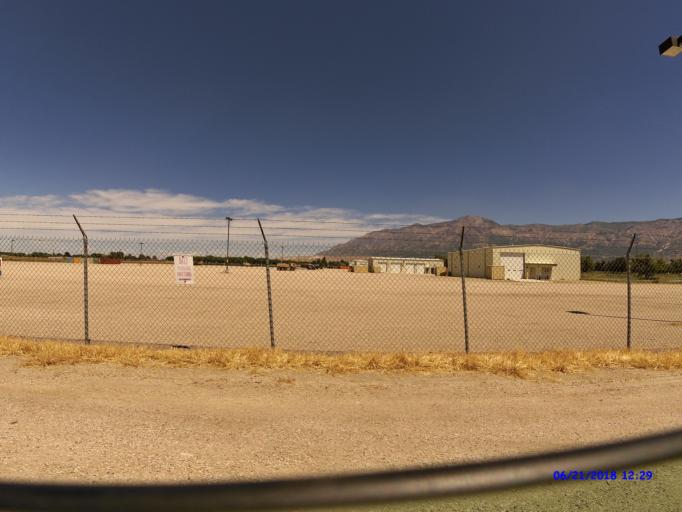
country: US
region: Utah
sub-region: Weber County
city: Harrisville
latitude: 41.2763
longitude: -112.0010
